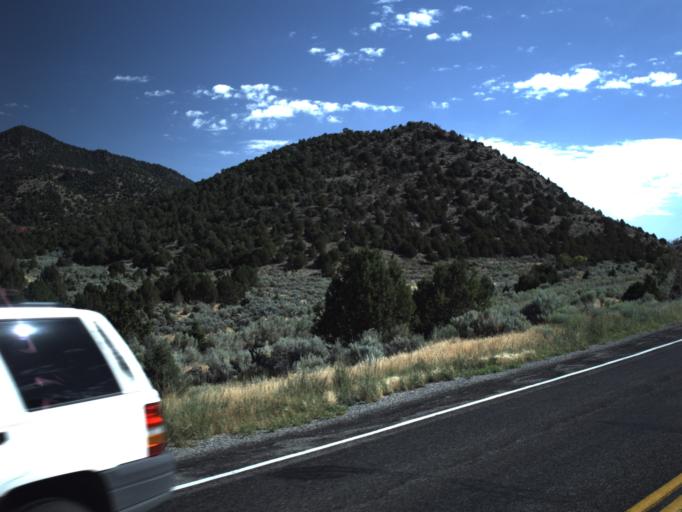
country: US
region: Utah
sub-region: Utah County
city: Genola
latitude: 39.9464
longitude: -112.1328
